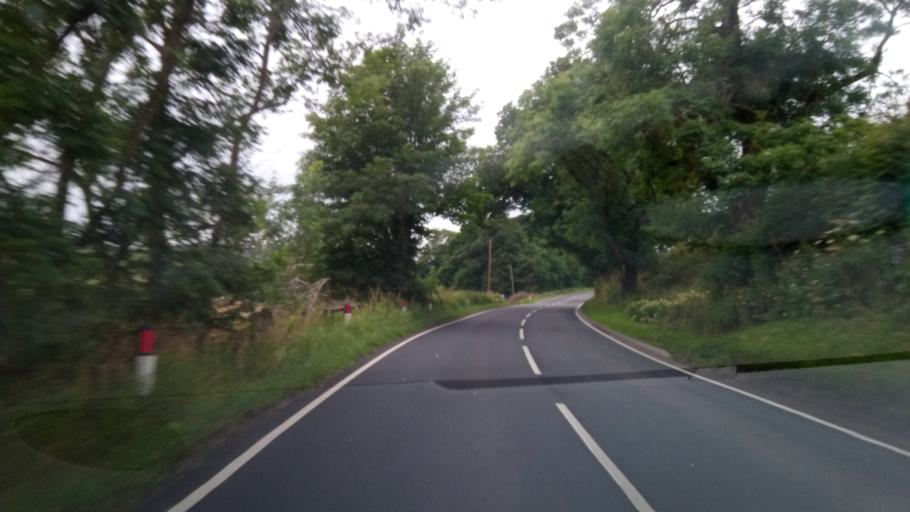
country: GB
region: Scotland
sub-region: The Scottish Borders
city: Hawick
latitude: 55.3777
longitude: -2.8724
